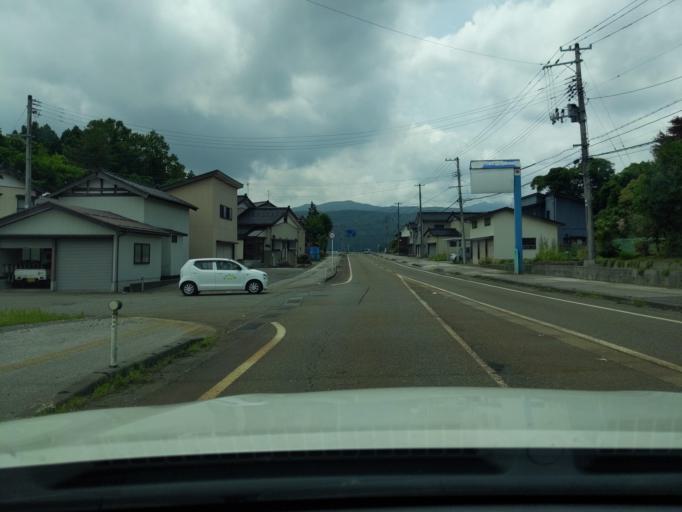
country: JP
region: Niigata
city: Kashiwazaki
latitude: 37.3314
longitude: 138.5765
